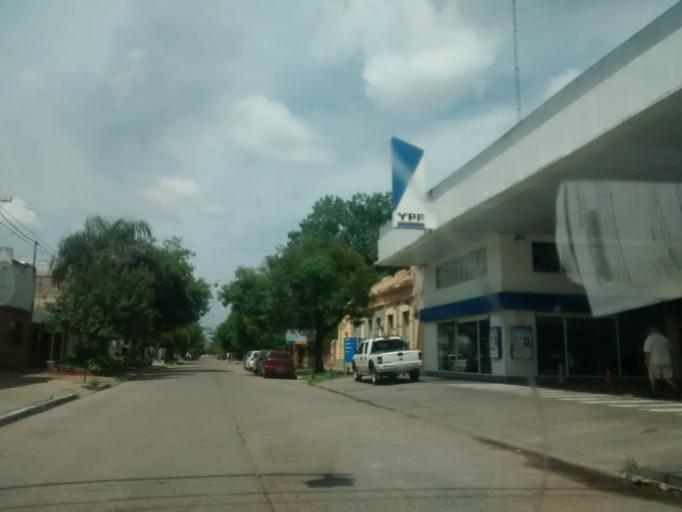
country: AR
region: Chaco
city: Resistencia
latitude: -27.4466
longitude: -58.9919
